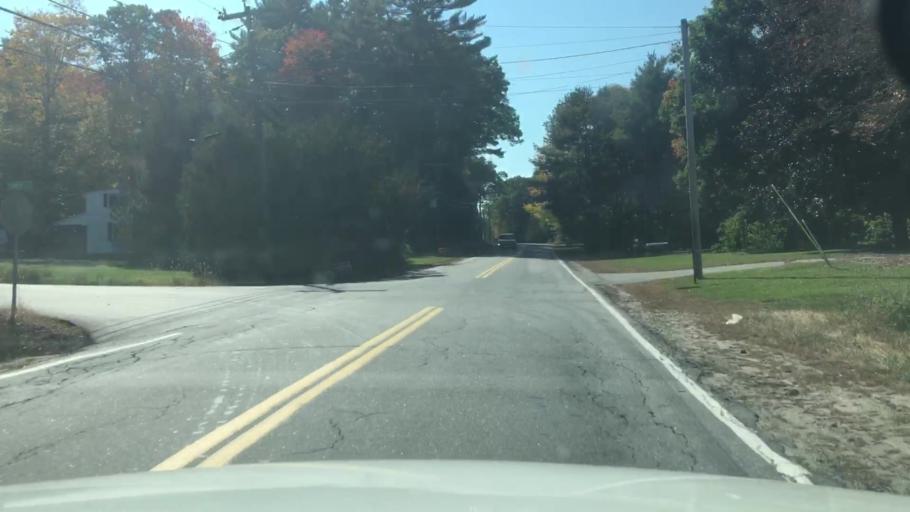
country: US
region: Maine
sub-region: Androscoggin County
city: Lisbon Falls
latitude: 44.0189
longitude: -70.0450
